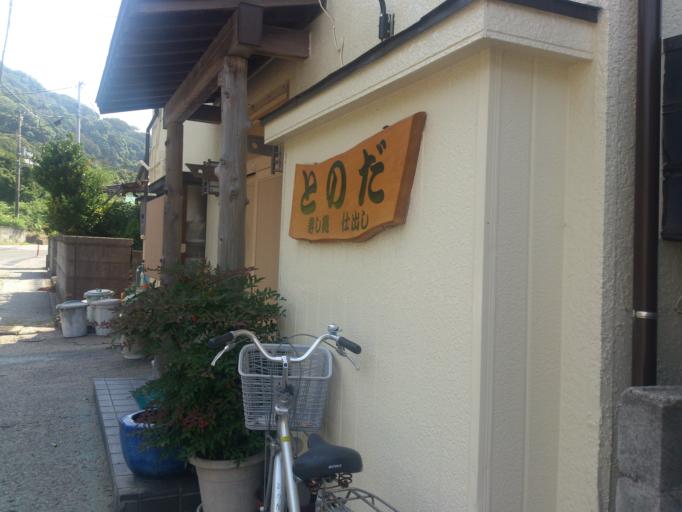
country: JP
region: Chiba
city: Tateyama
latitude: 35.0830
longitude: 139.8429
